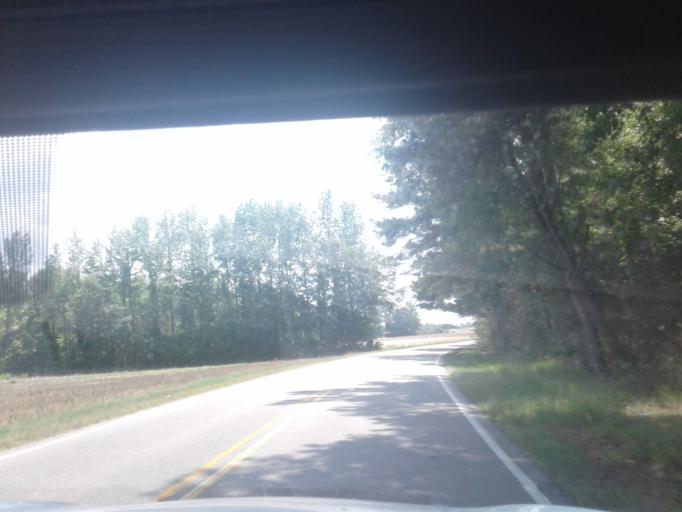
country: US
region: North Carolina
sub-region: Harnett County
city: Coats
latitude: 35.3830
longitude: -78.6181
